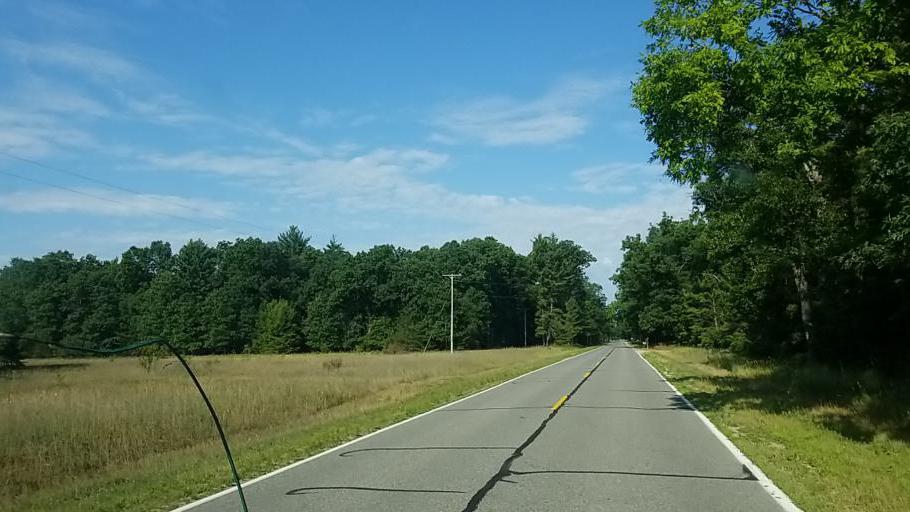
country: US
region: Michigan
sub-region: Muskegon County
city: Twin Lake
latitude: 43.4686
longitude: -86.1543
